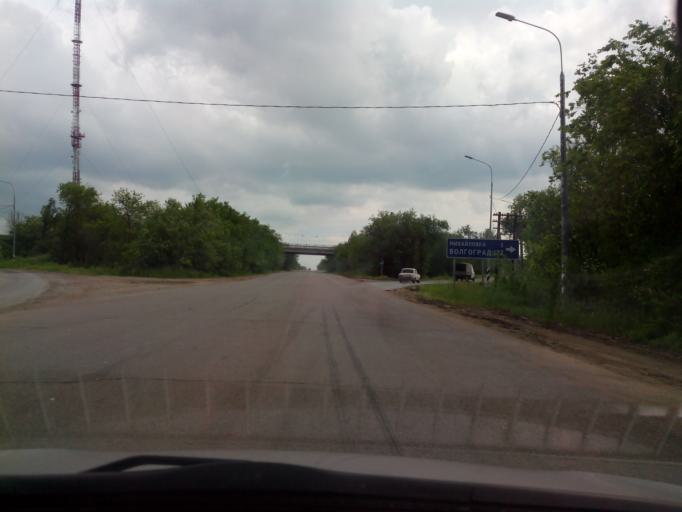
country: RU
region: Volgograd
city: Mikhaylovka
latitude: 50.0347
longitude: 43.1811
